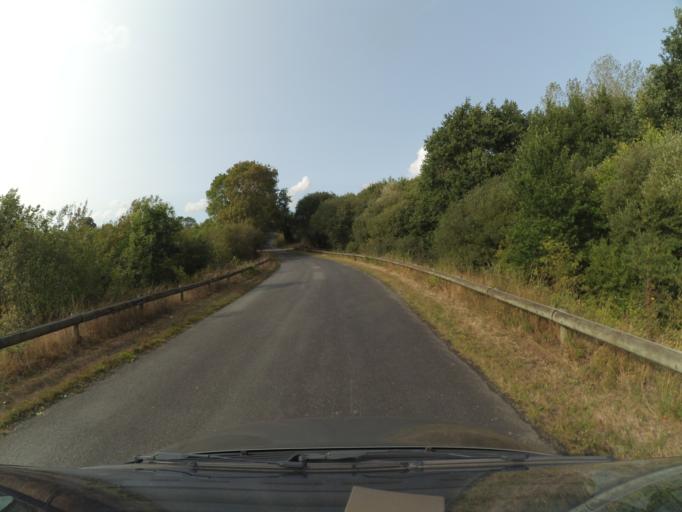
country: FR
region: Pays de la Loire
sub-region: Departement de la Vendee
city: Saint-Hilaire-de-Loulay
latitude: 46.9917
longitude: -1.3517
